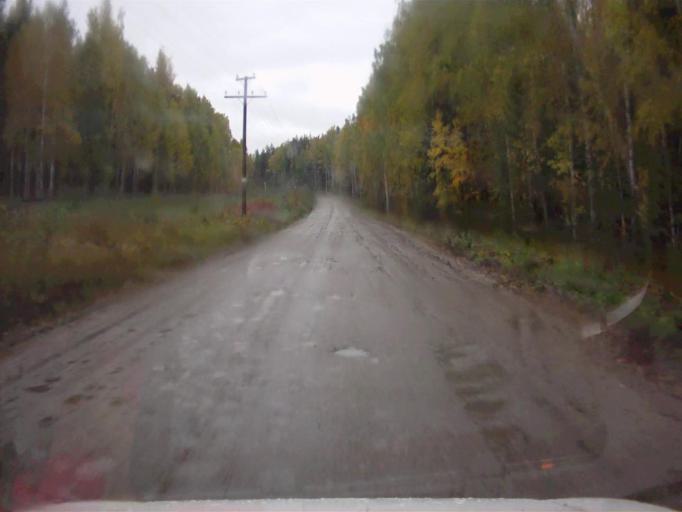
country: RU
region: Chelyabinsk
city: Kyshtym
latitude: 55.8033
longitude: 60.4799
